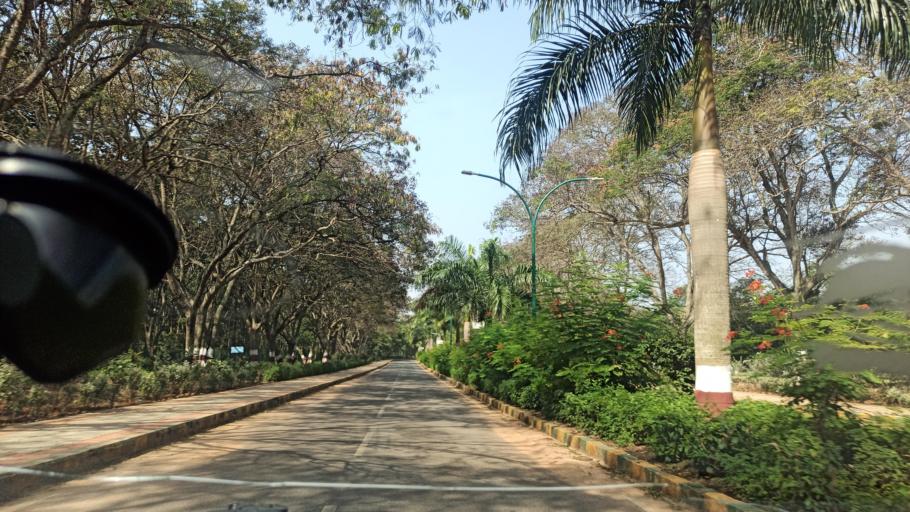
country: IN
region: Karnataka
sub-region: Bangalore Urban
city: Yelahanka
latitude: 13.0747
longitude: 77.5870
